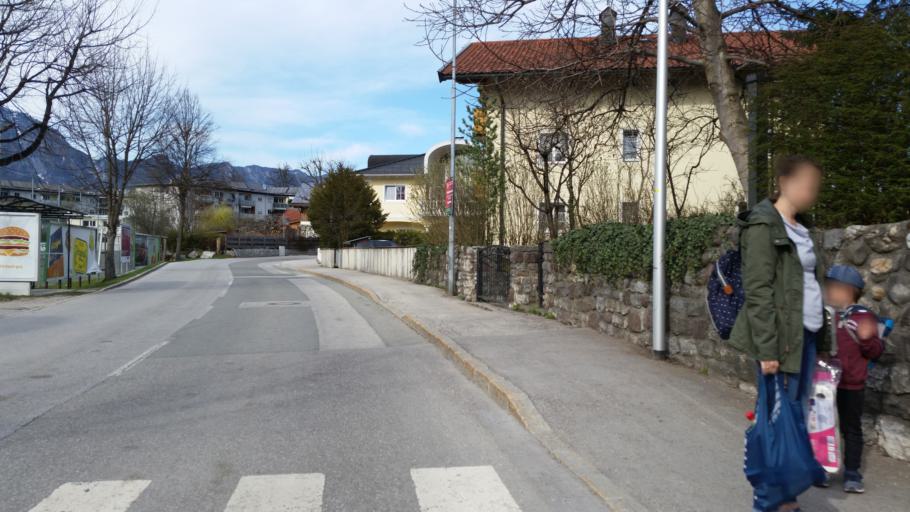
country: AT
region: Tyrol
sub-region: Politischer Bezirk Kufstein
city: Worgl
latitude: 47.4876
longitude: 12.0582
